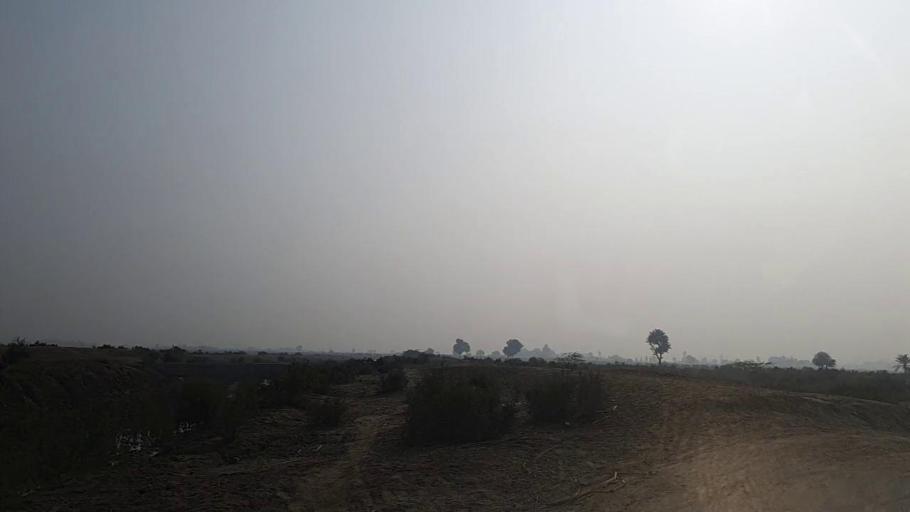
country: PK
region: Sindh
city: Sanghar
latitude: 26.0858
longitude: 68.9141
